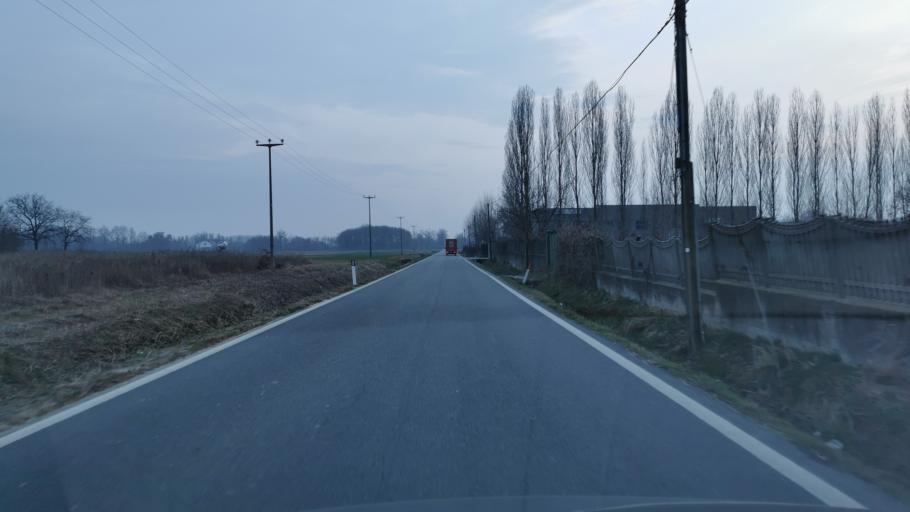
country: IT
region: Piedmont
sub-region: Provincia di Torino
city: Montalenghe
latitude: 45.3247
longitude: 7.8319
